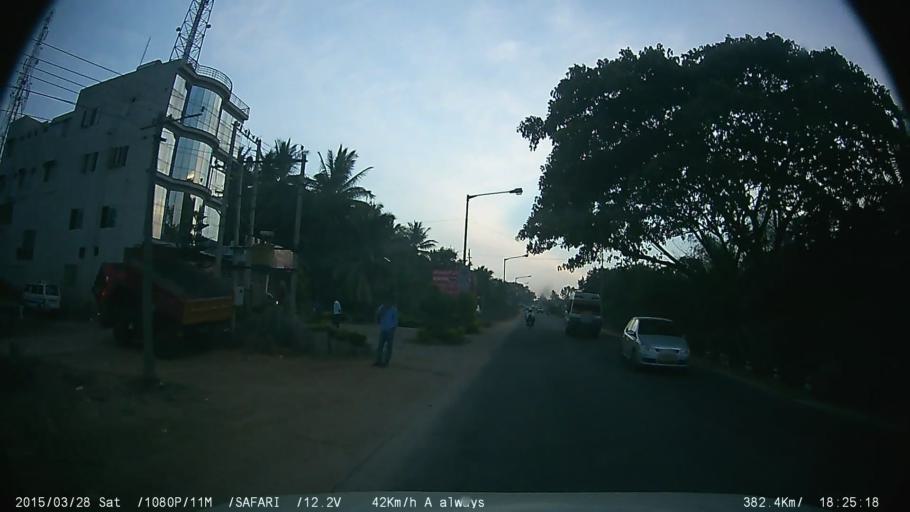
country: IN
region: Karnataka
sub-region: Mandya
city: Shrirangapattana
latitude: 12.4102
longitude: 76.5782
